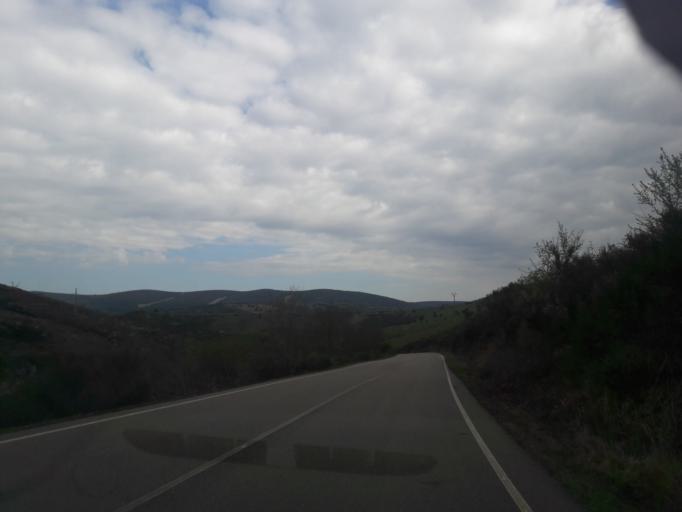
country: ES
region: Castille and Leon
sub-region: Provincia de Salamanca
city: Serradilla del Arroyo
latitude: 40.5102
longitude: -6.3625
